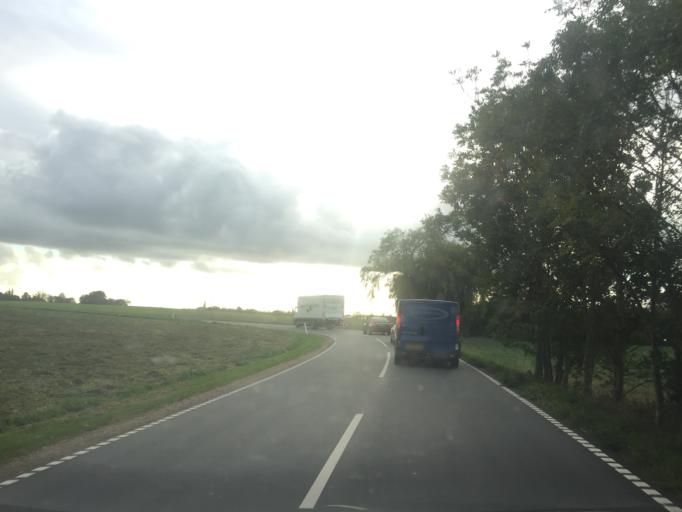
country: DK
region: Capital Region
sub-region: Hoje-Taastrup Kommune
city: Flong
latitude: 55.6707
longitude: 12.1818
